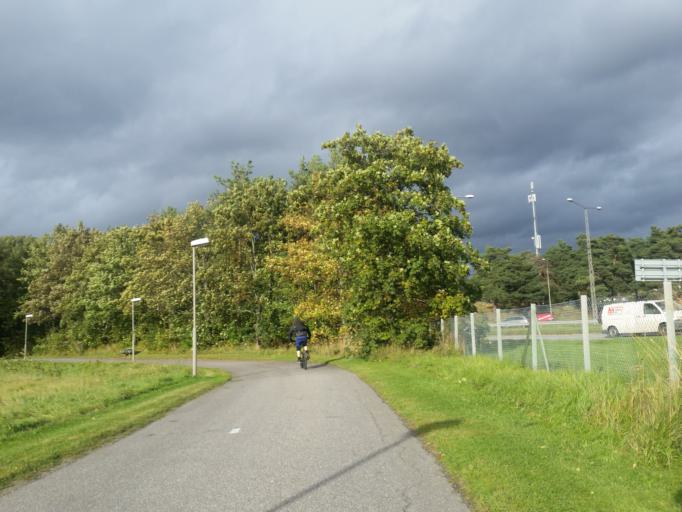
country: SE
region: Stockholm
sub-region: Stockholms Kommun
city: Arsta
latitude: 59.2620
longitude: 18.0978
